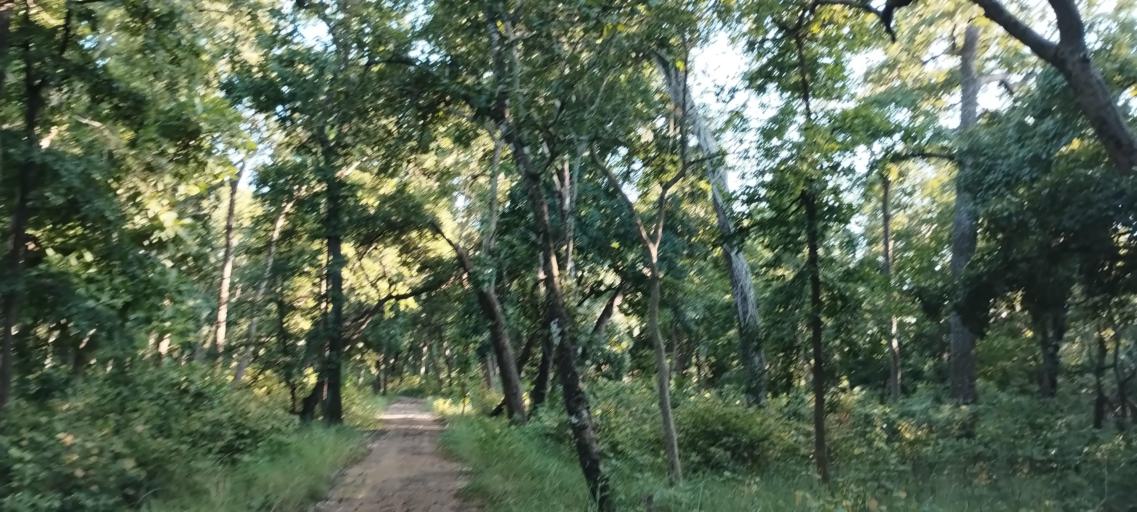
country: NP
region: Far Western
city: Tikapur
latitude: 28.4928
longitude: 81.2551
